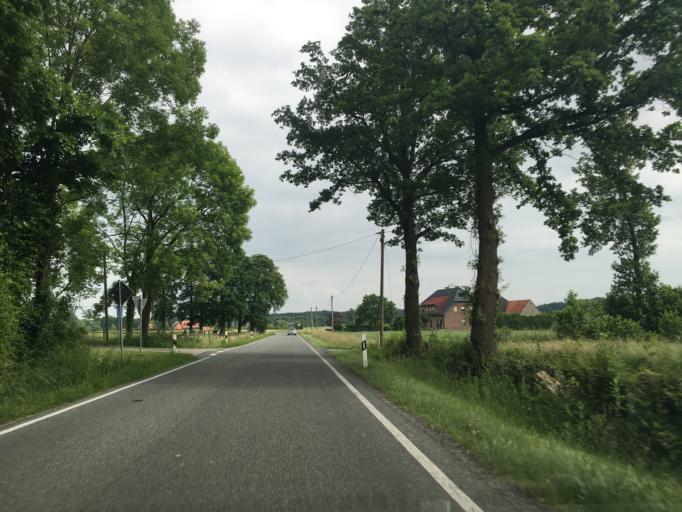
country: DE
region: North Rhine-Westphalia
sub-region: Regierungsbezirk Munster
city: Horstmar
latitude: 52.1012
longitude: 7.3187
